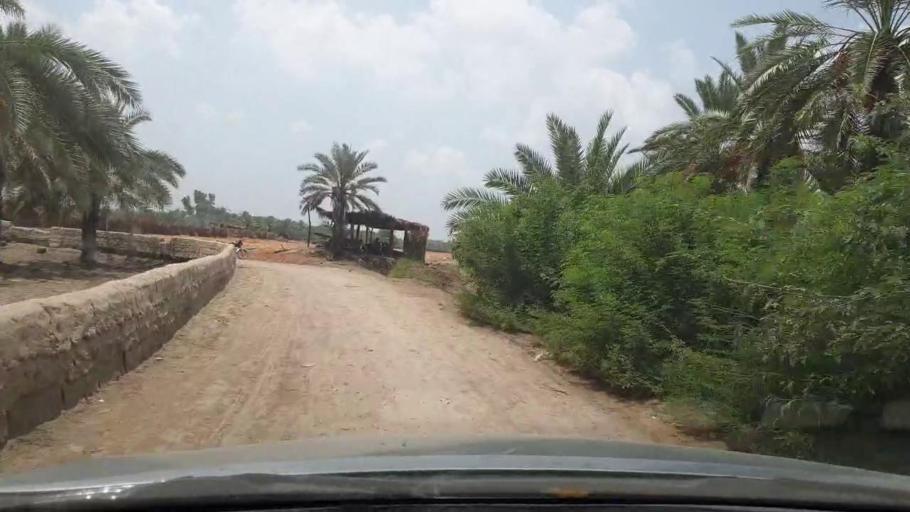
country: PK
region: Sindh
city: Khairpur
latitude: 27.4566
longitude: 68.7197
